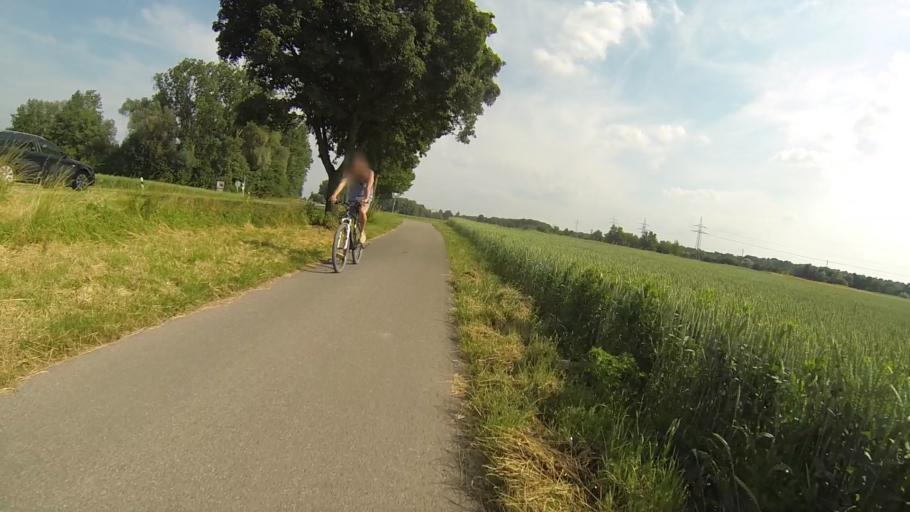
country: DE
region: Bavaria
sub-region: Swabia
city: Neu-Ulm
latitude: 48.3606
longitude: 10.0123
